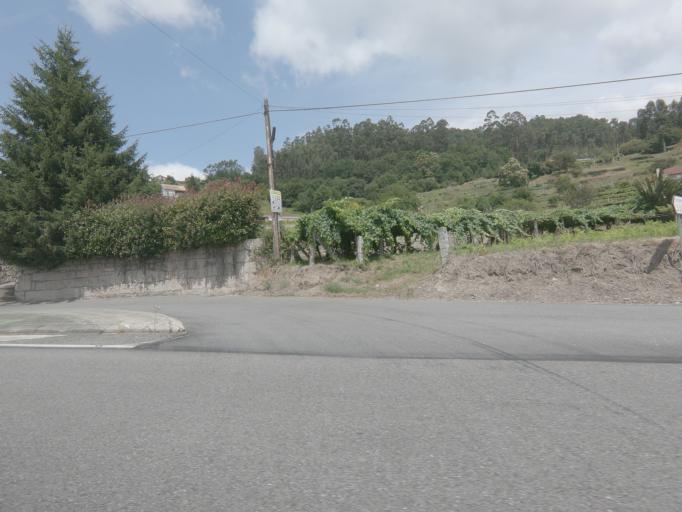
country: ES
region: Galicia
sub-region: Provincia de Pontevedra
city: Tomino
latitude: 42.0409
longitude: -8.7282
